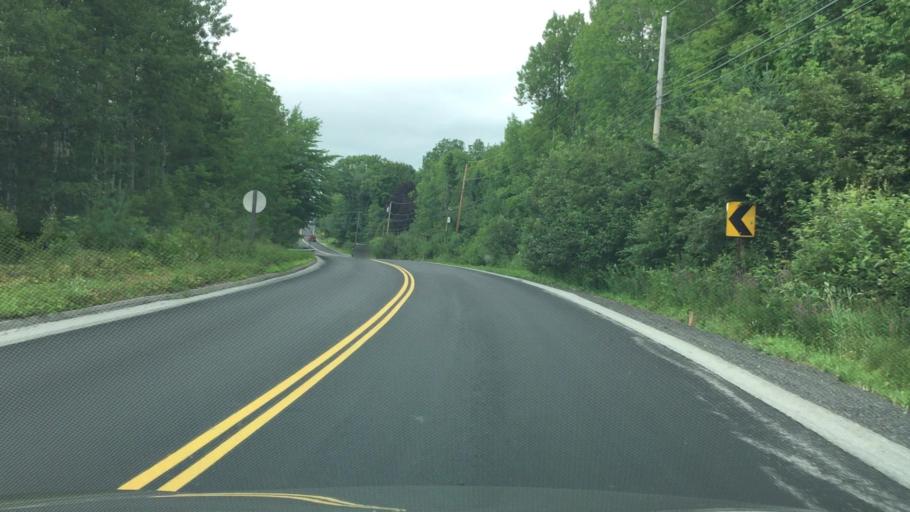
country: US
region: Maine
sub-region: Waldo County
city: Winterport
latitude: 44.6175
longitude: -68.8274
